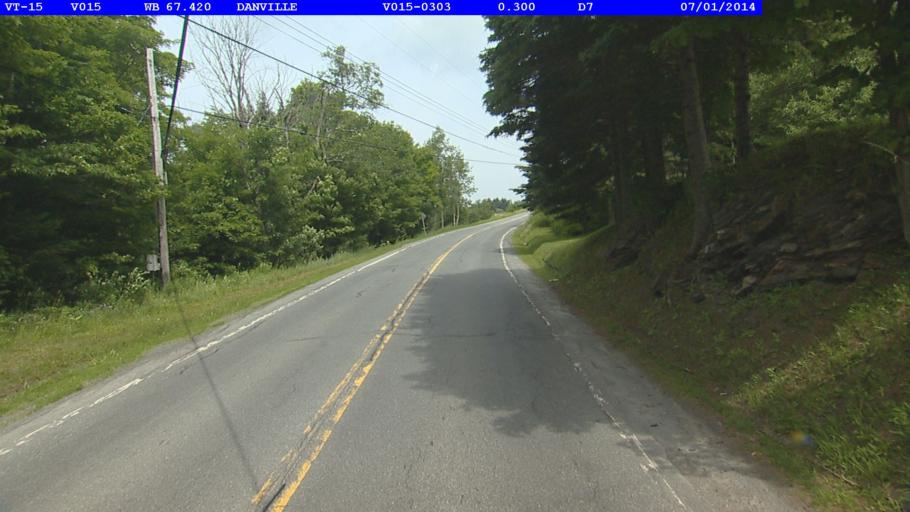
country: US
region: Vermont
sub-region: Caledonia County
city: Hardwick
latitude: 44.4185
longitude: -72.2173
